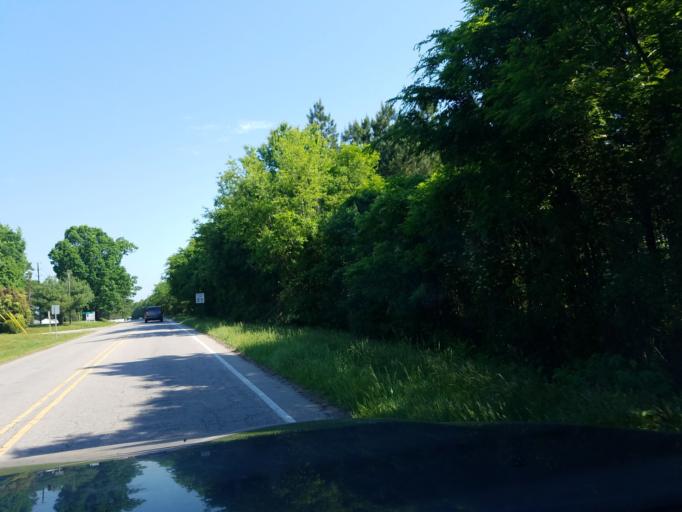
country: US
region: North Carolina
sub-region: Vance County
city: Henderson
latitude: 36.3409
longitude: -78.4472
